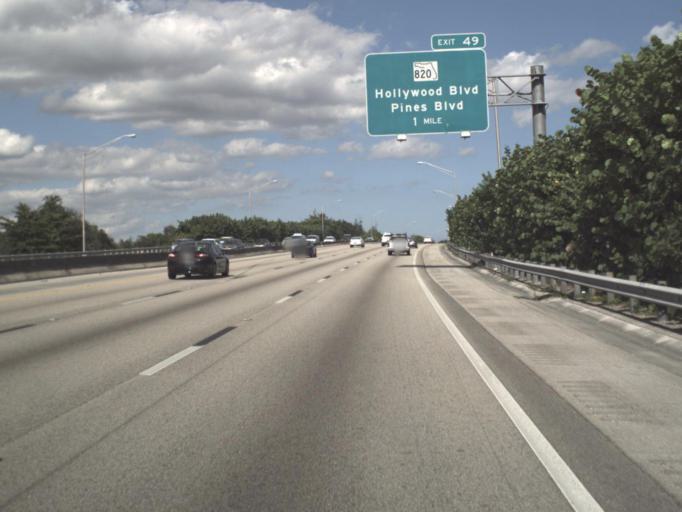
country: US
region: Florida
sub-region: Broward County
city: Miramar
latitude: 25.9925
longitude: -80.2264
